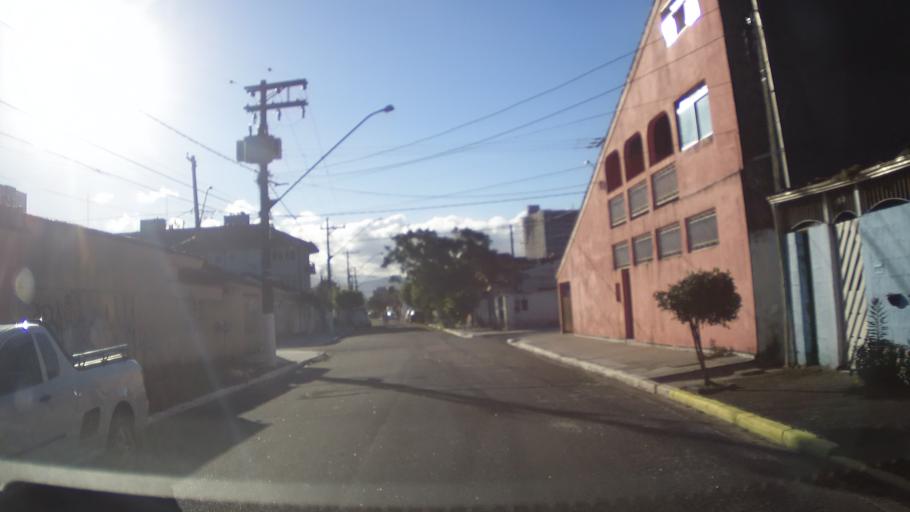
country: BR
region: Sao Paulo
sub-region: Praia Grande
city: Praia Grande
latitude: -24.0102
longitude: -46.3950
